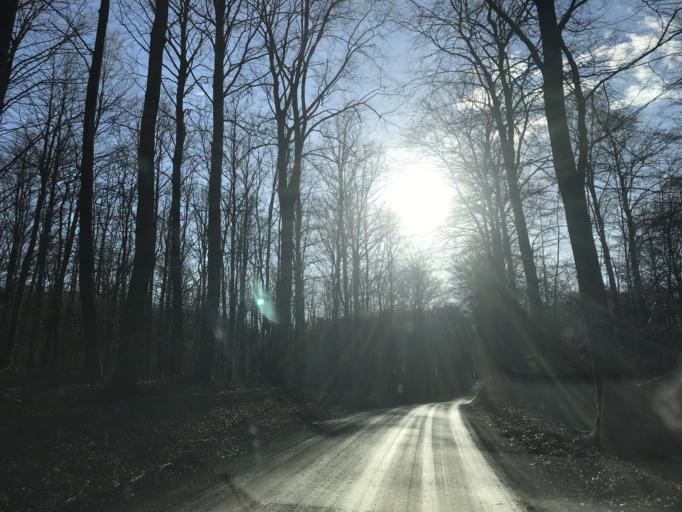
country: SE
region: Skane
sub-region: Ystads Kommun
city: Ystad
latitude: 55.5594
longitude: 13.8221
